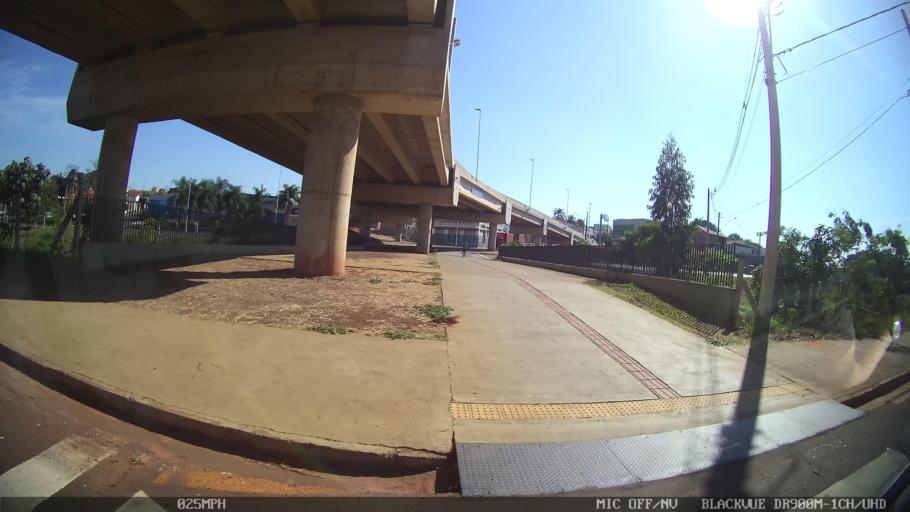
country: BR
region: Sao Paulo
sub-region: Sao Jose Do Rio Preto
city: Sao Jose do Rio Preto
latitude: -20.7892
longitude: -49.3885
